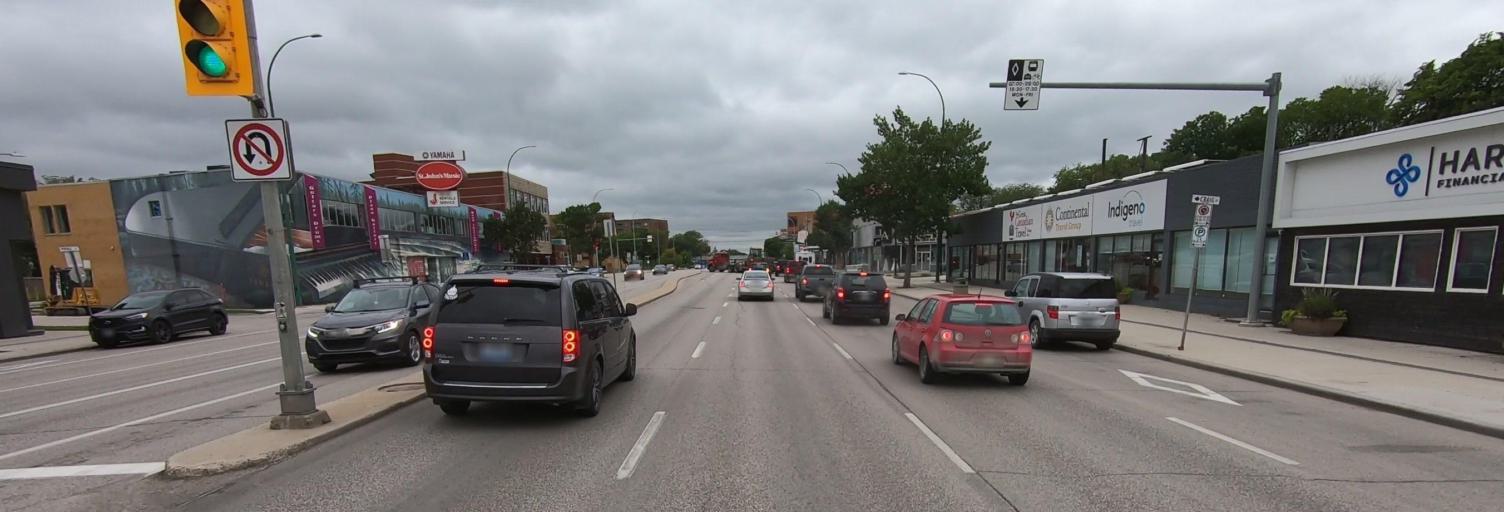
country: CA
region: Manitoba
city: Winnipeg
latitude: 49.8826
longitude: -97.1892
